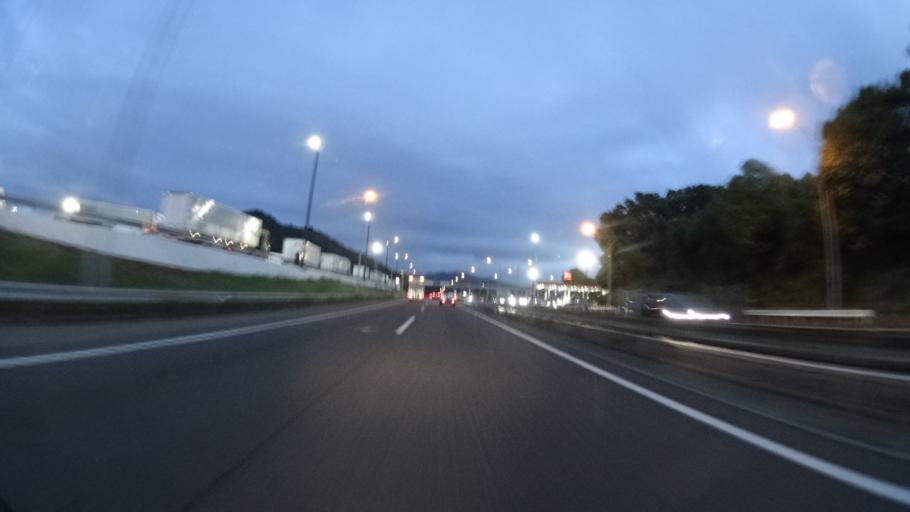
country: JP
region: Shiga Prefecture
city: Hikone
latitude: 35.2211
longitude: 136.2832
